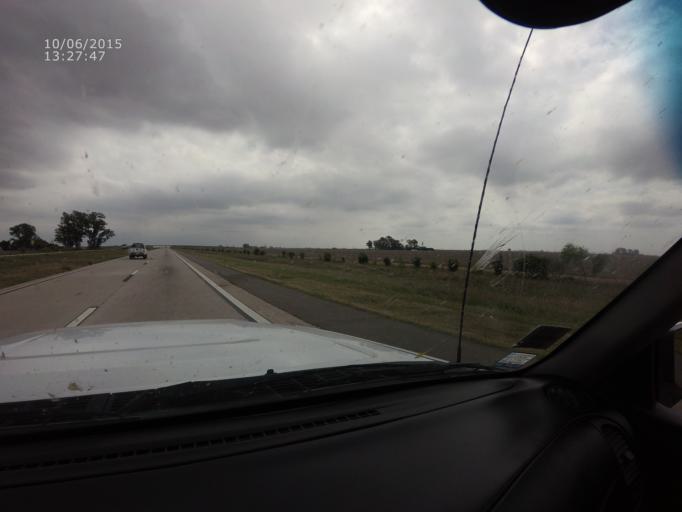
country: AR
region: Cordoba
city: Leones
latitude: -32.6445
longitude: -62.2097
